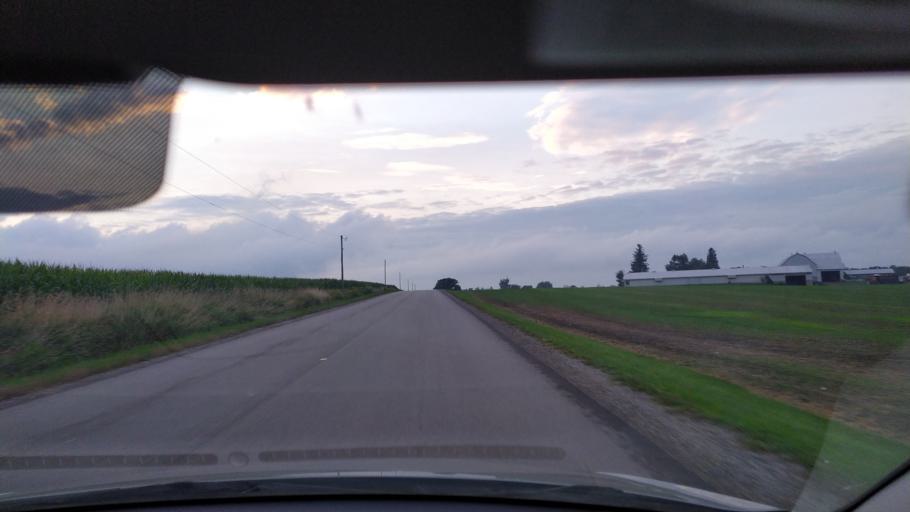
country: CA
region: Ontario
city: Kitchener
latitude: 43.3358
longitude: -80.6270
